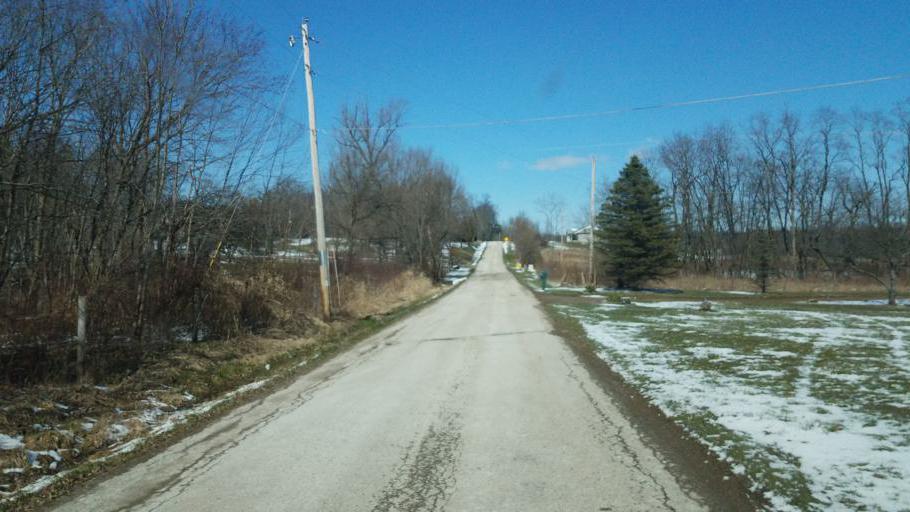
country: US
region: Ohio
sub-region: Richland County
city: Lexington
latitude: 40.6396
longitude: -82.6251
